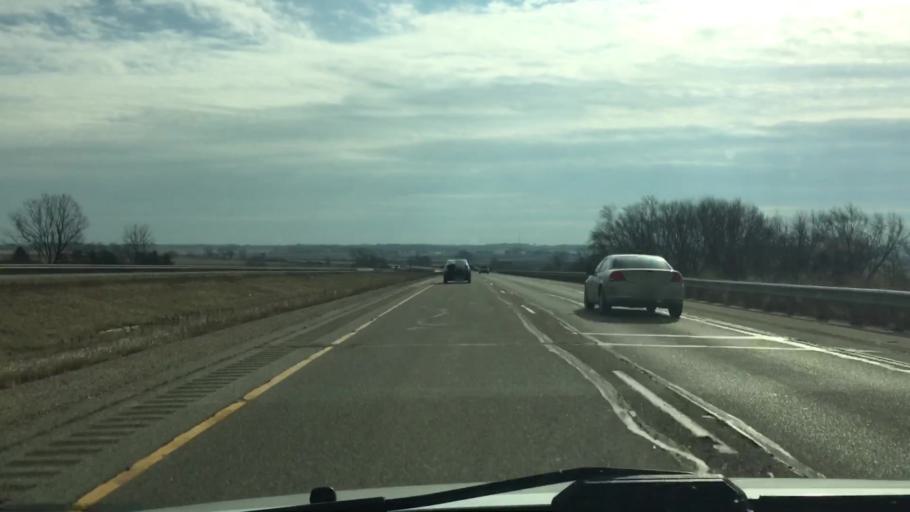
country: US
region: Wisconsin
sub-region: Walworth County
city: Elkhorn
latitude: 42.6545
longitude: -88.5085
